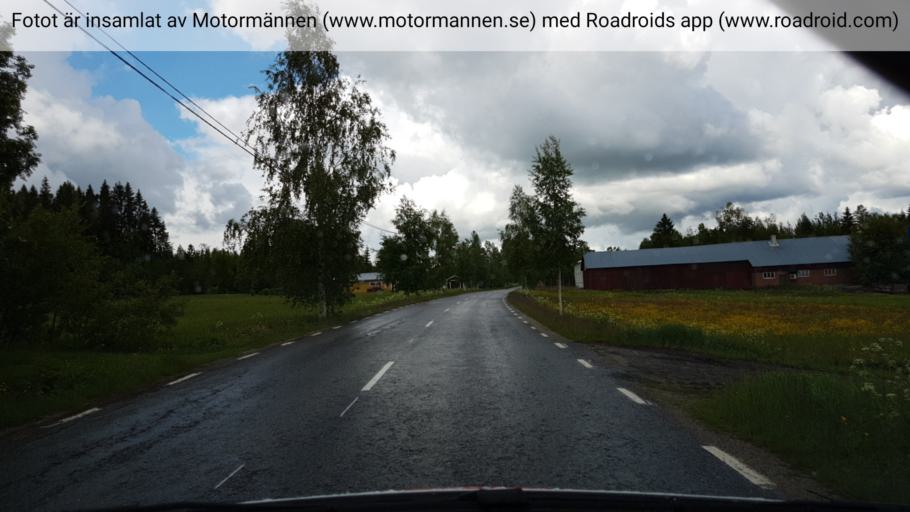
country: SE
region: Vaesterbotten
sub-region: Vannas Kommun
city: Vannasby
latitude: 63.8656
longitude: 19.8984
